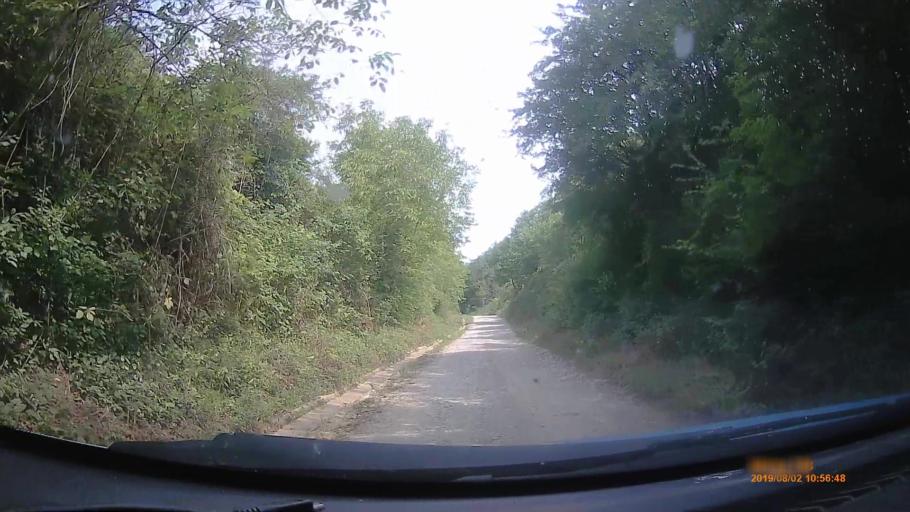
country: HU
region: Baranya
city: Buekkoesd
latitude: 46.0975
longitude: 17.9515
